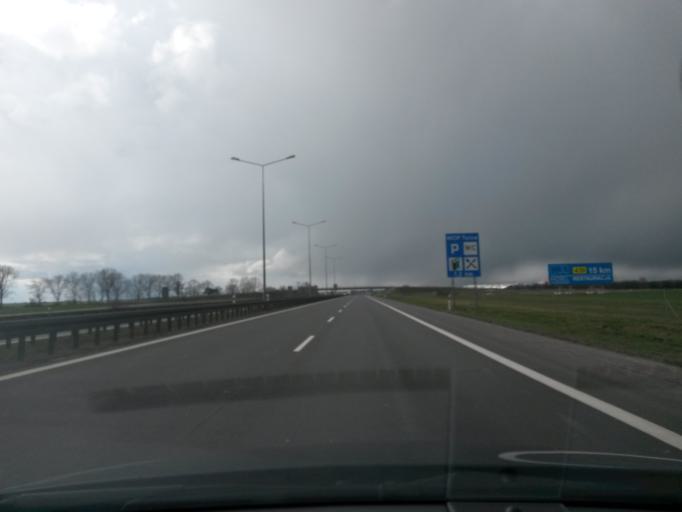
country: PL
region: Greater Poland Voivodeship
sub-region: Powiat poznanski
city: Kleszczewo
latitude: 52.3222
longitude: 17.1146
